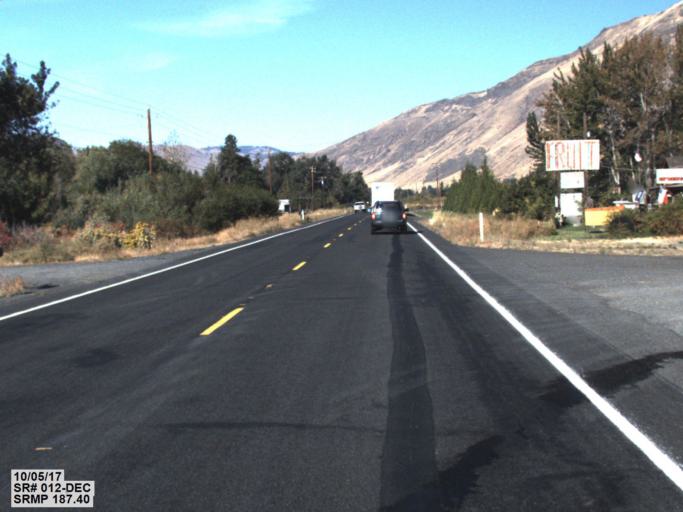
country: US
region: Washington
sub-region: Yakima County
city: Tieton
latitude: 46.7417
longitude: -120.7484
